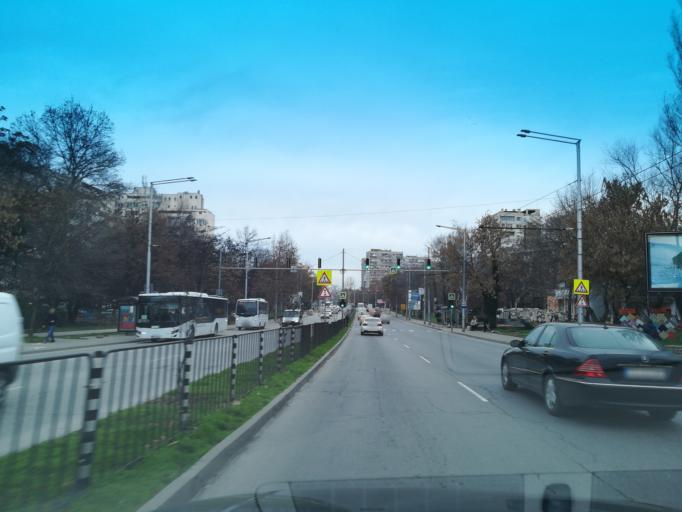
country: BG
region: Plovdiv
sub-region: Obshtina Plovdiv
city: Plovdiv
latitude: 42.1558
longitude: 24.7312
